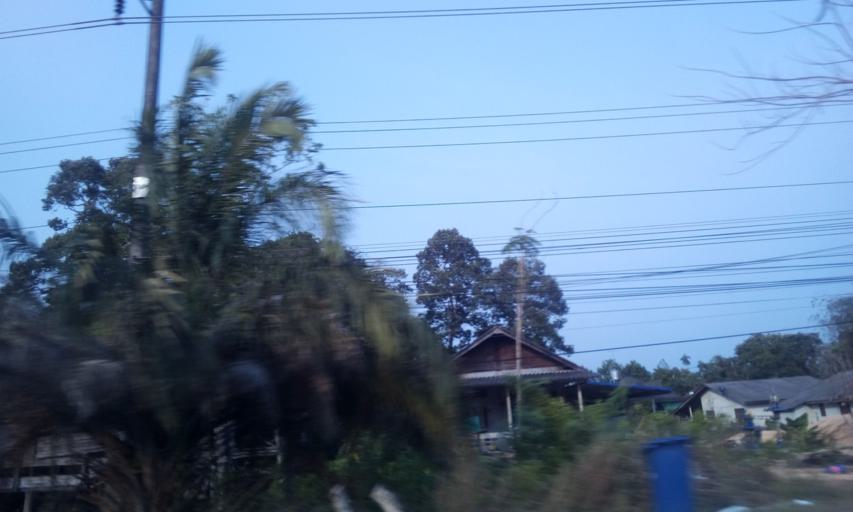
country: TH
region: Chanthaburi
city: Khlung
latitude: 12.4226
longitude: 102.3221
